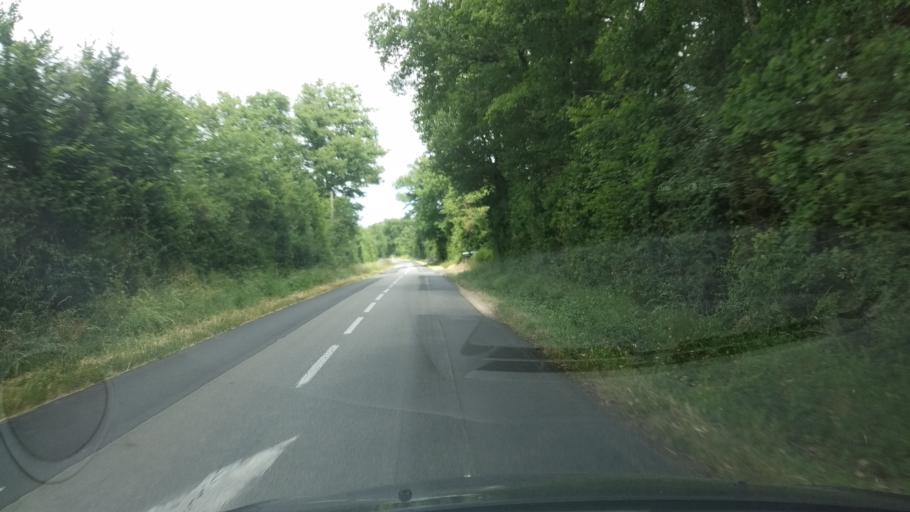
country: FR
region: Poitou-Charentes
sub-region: Departement de la Vienne
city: Vouneuil-sous-Biard
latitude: 46.5649
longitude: 0.2685
